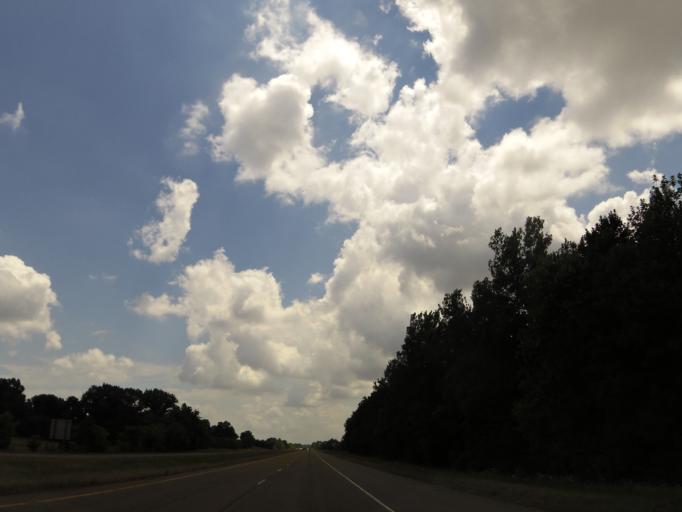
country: US
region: Tennessee
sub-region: Dyer County
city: Dyersburg
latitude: 36.0153
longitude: -89.3412
